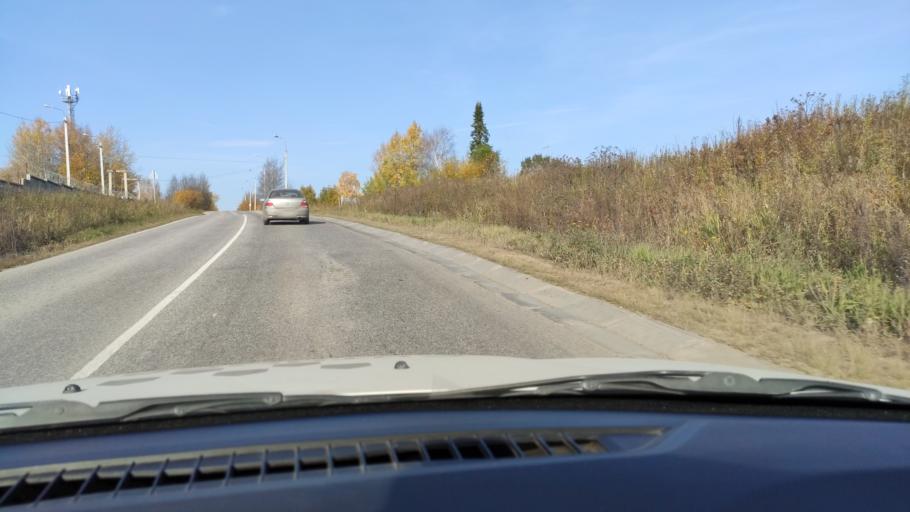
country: RU
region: Perm
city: Novyye Lyady
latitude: 58.0439
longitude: 56.5947
